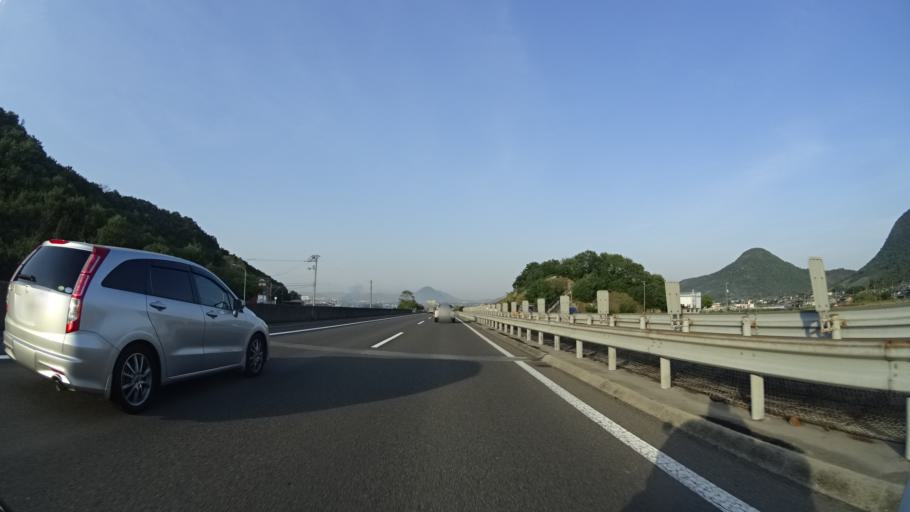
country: JP
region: Kagawa
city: Tadotsu
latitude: 34.2277
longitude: 133.7393
